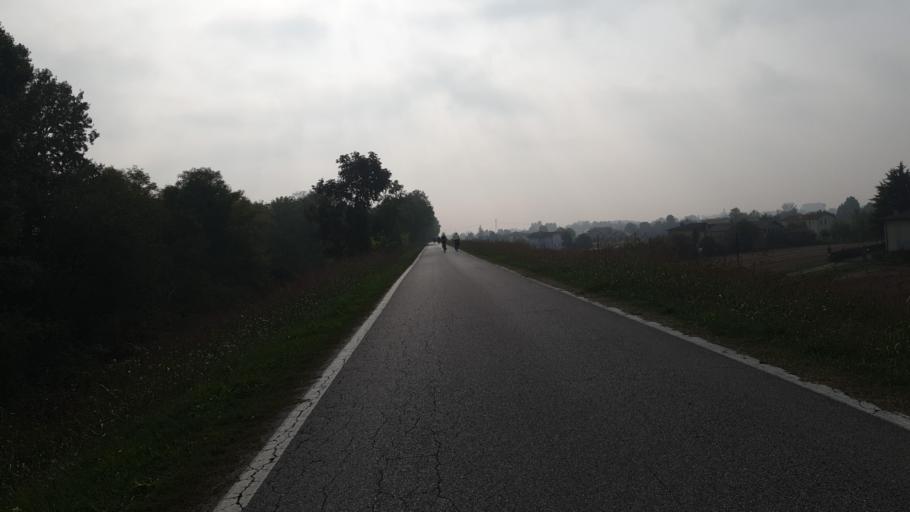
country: IT
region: Veneto
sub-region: Provincia di Venezia
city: Galta
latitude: 45.3777
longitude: 12.0226
